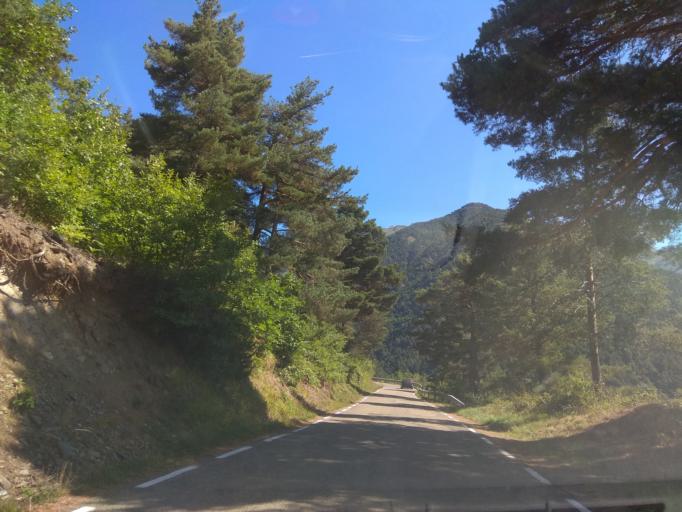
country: ES
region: Catalonia
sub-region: Provincia de Lleida
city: Vielha
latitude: 42.7409
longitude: 0.7512
